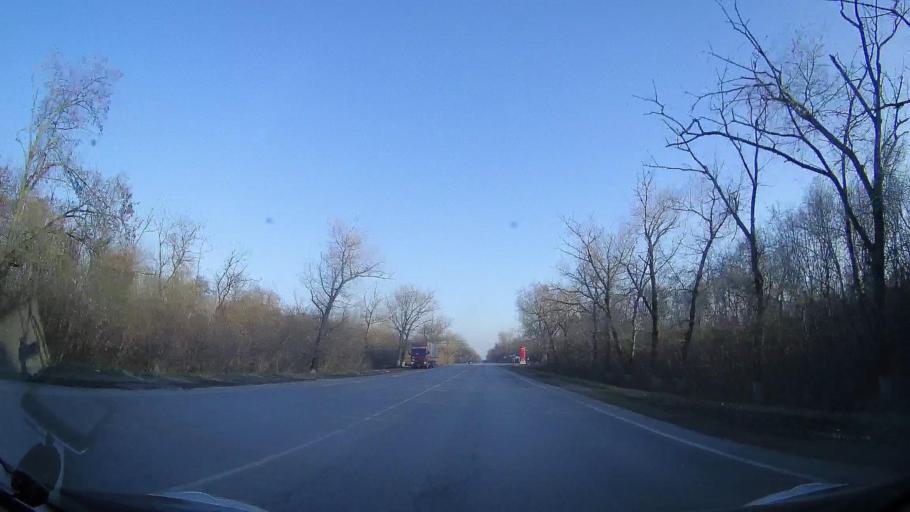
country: RU
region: Rostov
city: Bataysk
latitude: 47.0493
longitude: 39.8401
